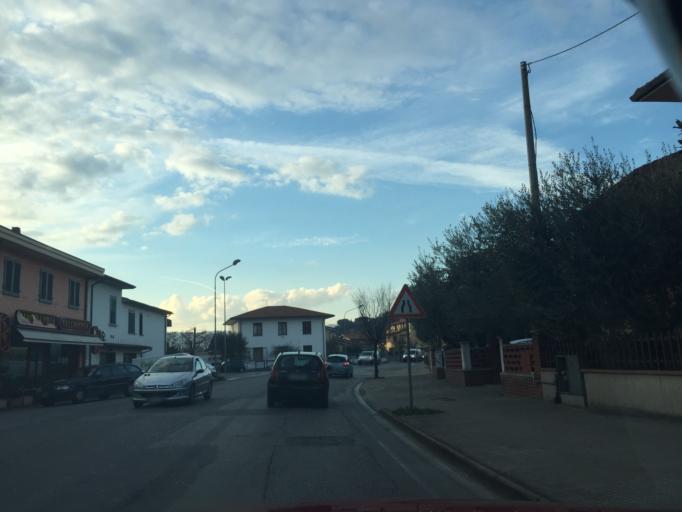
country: IT
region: Tuscany
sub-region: Provincia di Pistoia
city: Pieve a Nievole
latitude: 43.8747
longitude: 10.8012
